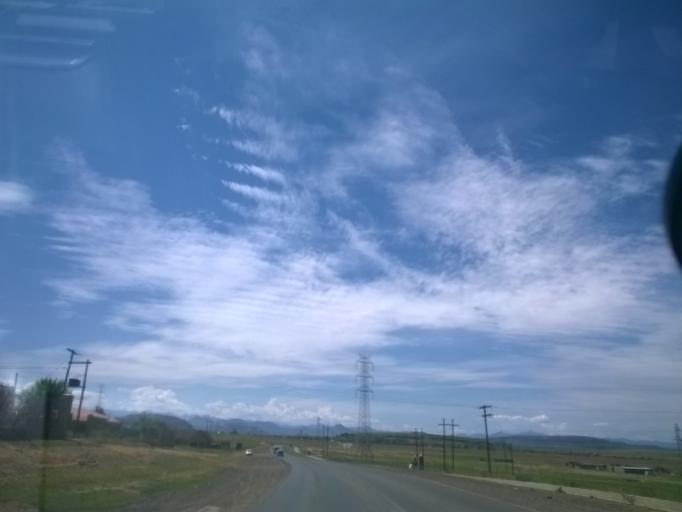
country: LS
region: Leribe
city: Maputsoe
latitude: -28.9165
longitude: 27.9248
